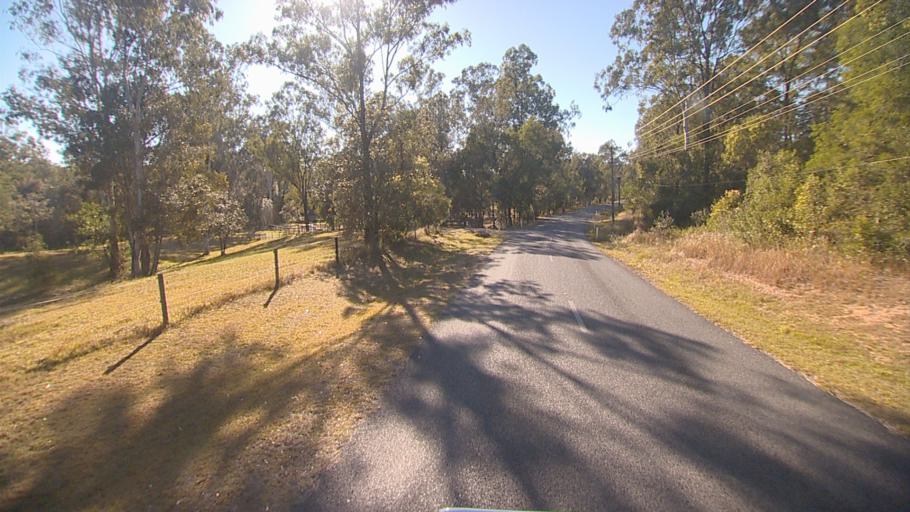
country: AU
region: Queensland
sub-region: Logan
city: North Maclean
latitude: -27.7838
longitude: 152.9728
